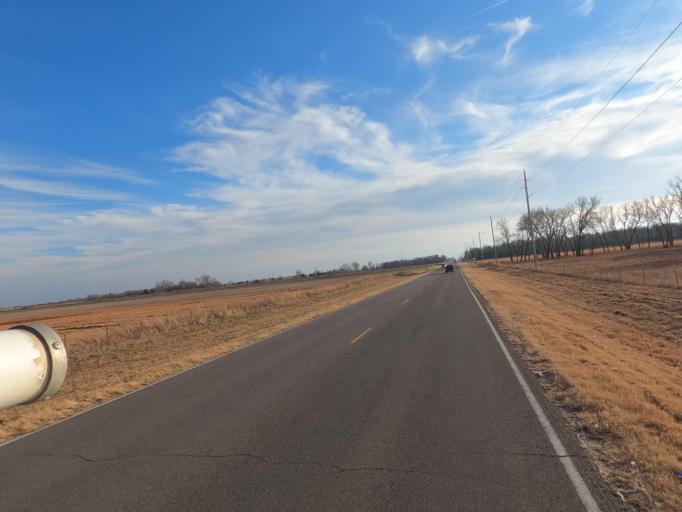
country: US
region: Kansas
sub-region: Reno County
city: Buhler
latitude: 38.0405
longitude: -97.7753
